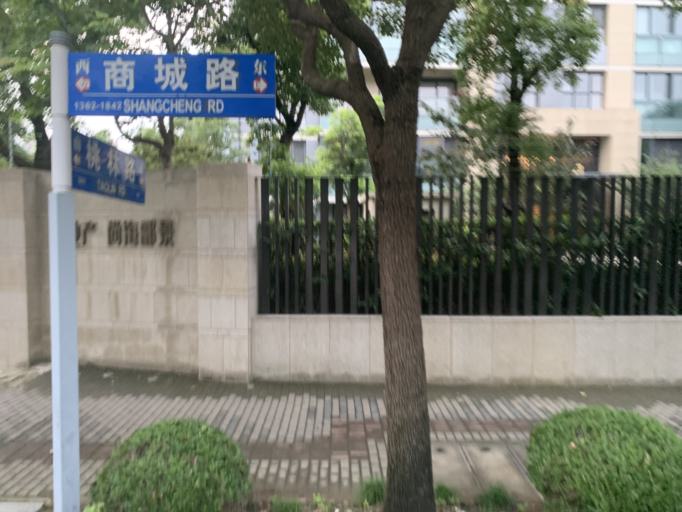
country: CN
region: Shanghai Shi
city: Pudong
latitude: 31.2399
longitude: 121.5322
